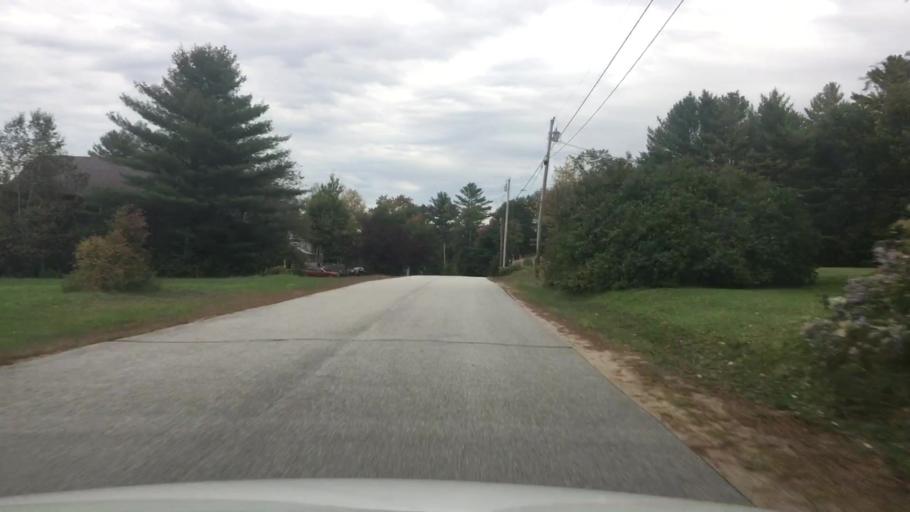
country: US
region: Maine
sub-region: Oxford County
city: Bethel
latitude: 44.4812
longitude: -70.7546
